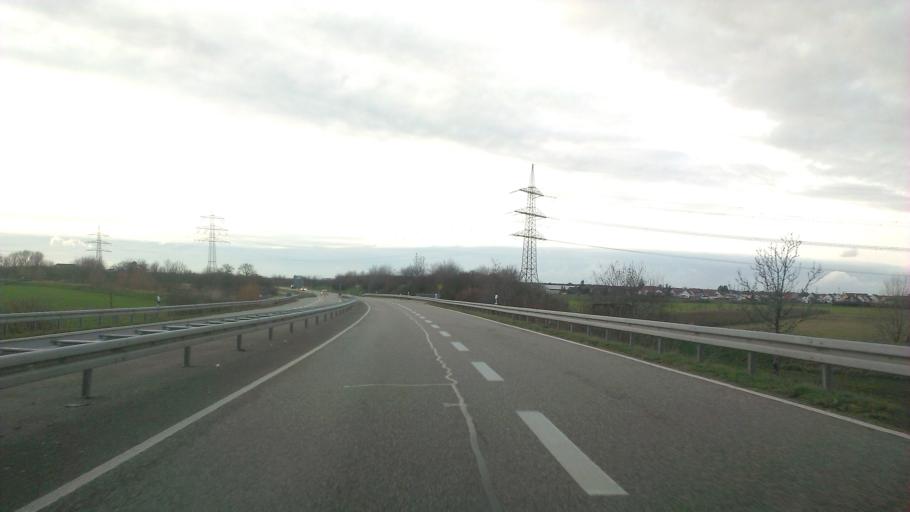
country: DE
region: Baden-Wuerttemberg
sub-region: Karlsruhe Region
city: Bruchsal
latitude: 49.1449
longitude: 8.6000
